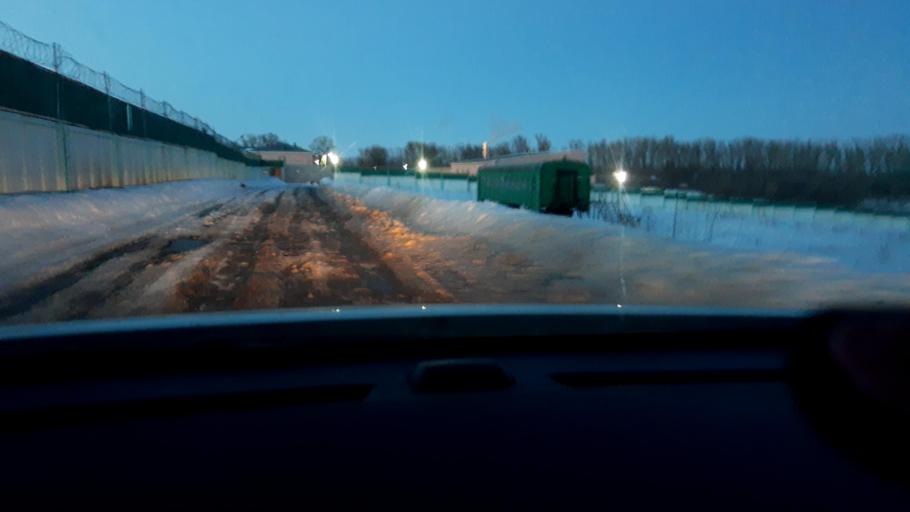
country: RU
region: Bashkortostan
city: Avdon
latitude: 54.3883
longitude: 55.6961
